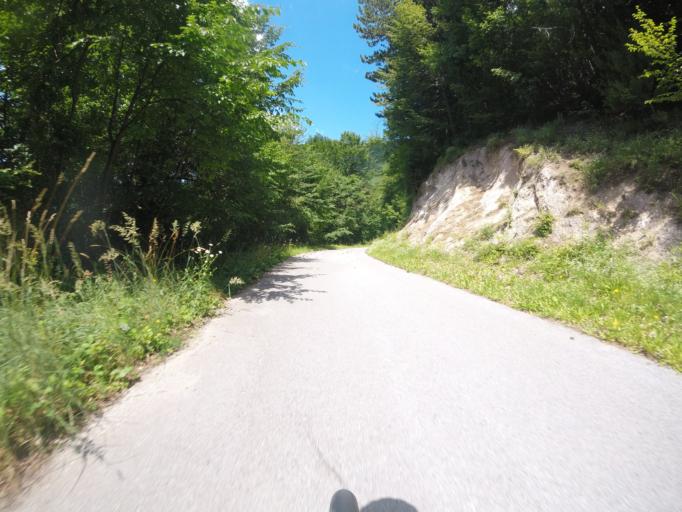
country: SI
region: Kostanjevica na Krki
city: Kostanjevica na Krki
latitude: 45.7693
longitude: 15.4180
